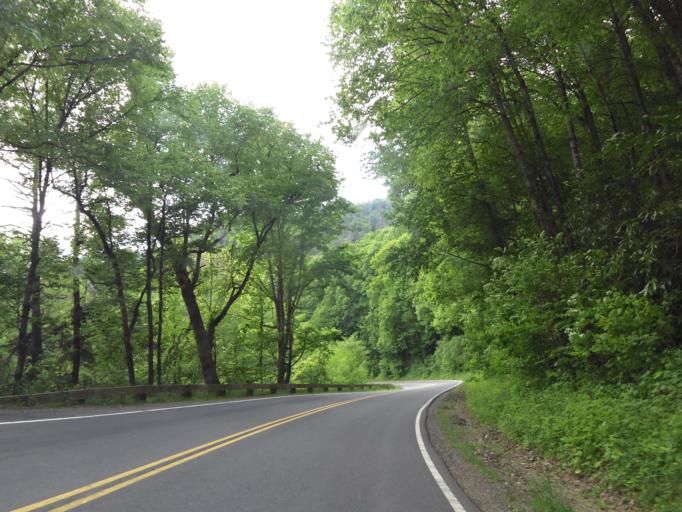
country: US
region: Tennessee
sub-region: Sevier County
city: Gatlinburg
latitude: 35.6368
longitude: -83.4636
